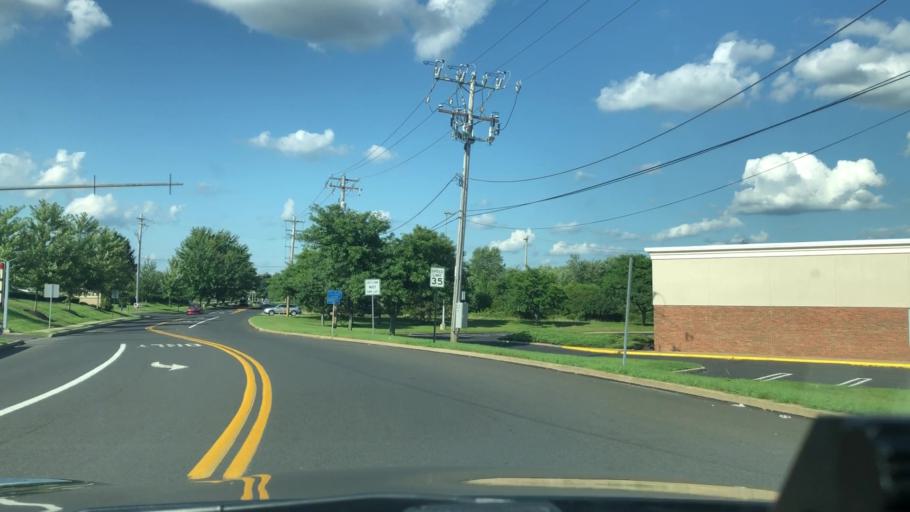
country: US
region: Pennsylvania
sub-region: Montgomery County
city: Montgomeryville
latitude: 40.2417
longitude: -75.2421
